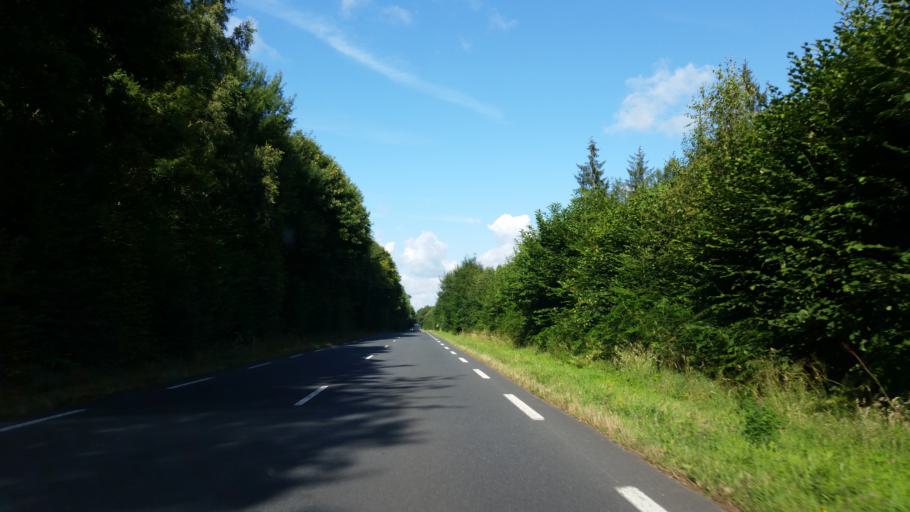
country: FR
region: Lower Normandy
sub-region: Departement du Calvados
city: Saint-Gatien-des-Bois
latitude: 49.3455
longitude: 0.1479
